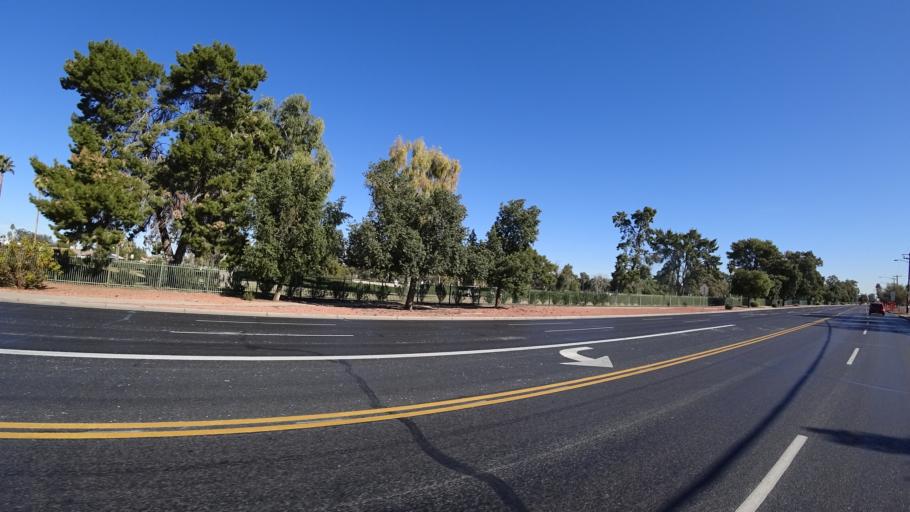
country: US
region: Arizona
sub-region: Maricopa County
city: Glendale
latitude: 33.4949
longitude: -112.1948
